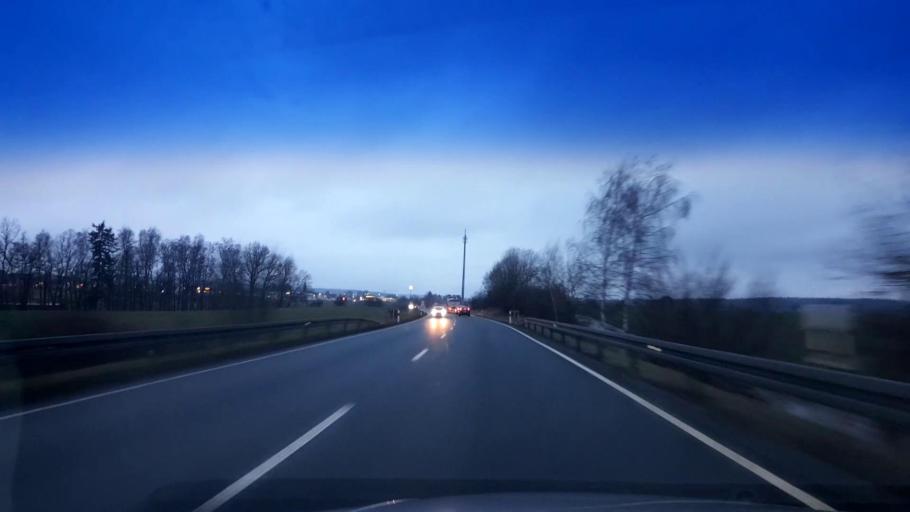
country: DE
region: Bavaria
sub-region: Upper Franconia
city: Speichersdorf
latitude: 49.8797
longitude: 11.7845
